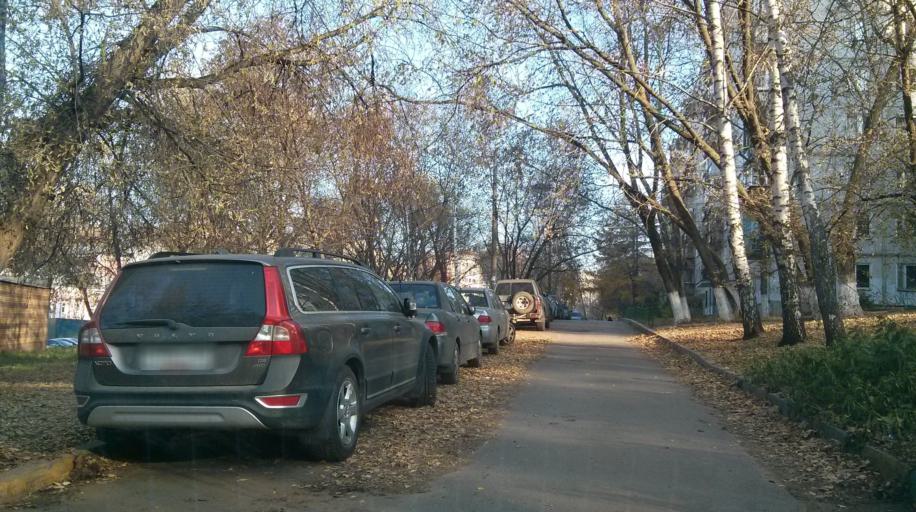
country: RU
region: Nizjnij Novgorod
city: Nizhniy Novgorod
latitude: 56.3206
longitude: 44.0217
